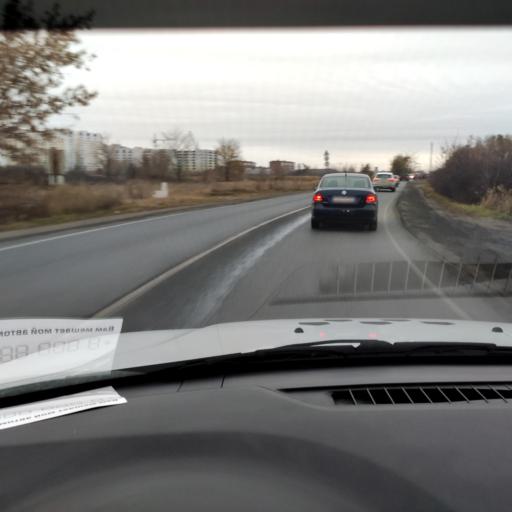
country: RU
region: Samara
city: Tol'yatti
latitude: 53.5139
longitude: 49.2456
